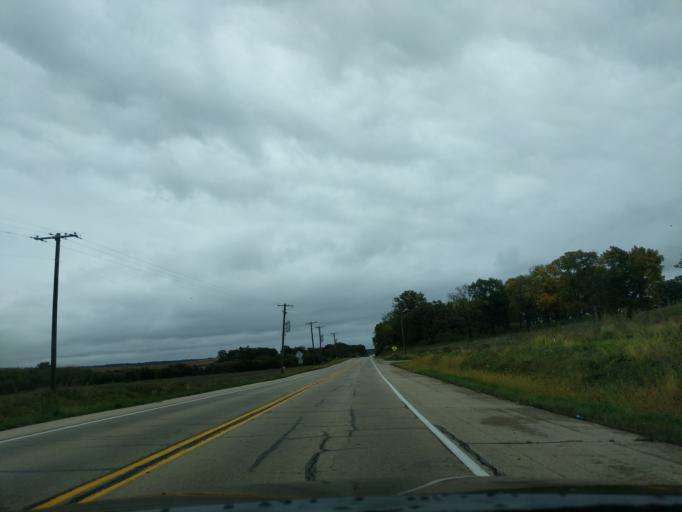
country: US
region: Illinois
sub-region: Ogle County
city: Oregon
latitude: 42.0033
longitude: -89.3741
